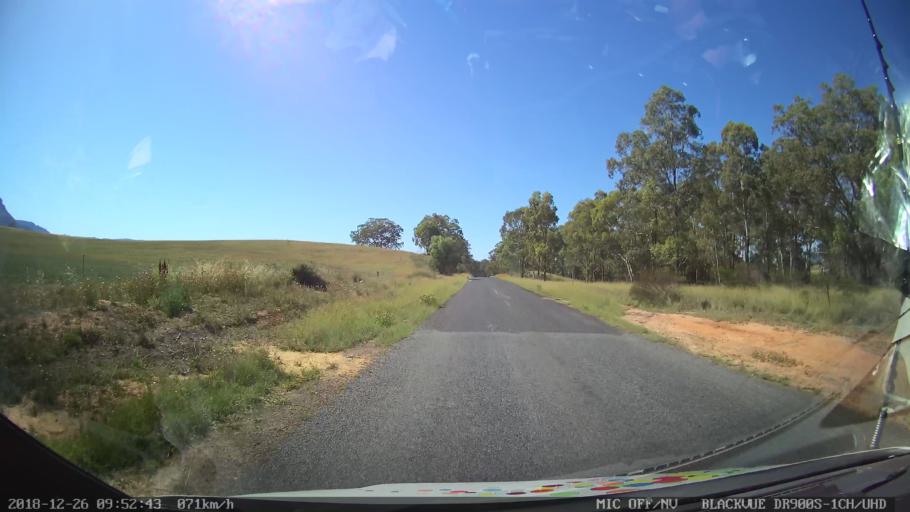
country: AU
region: New South Wales
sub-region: Mid-Western Regional
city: Kandos
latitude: -33.0136
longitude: 150.1501
